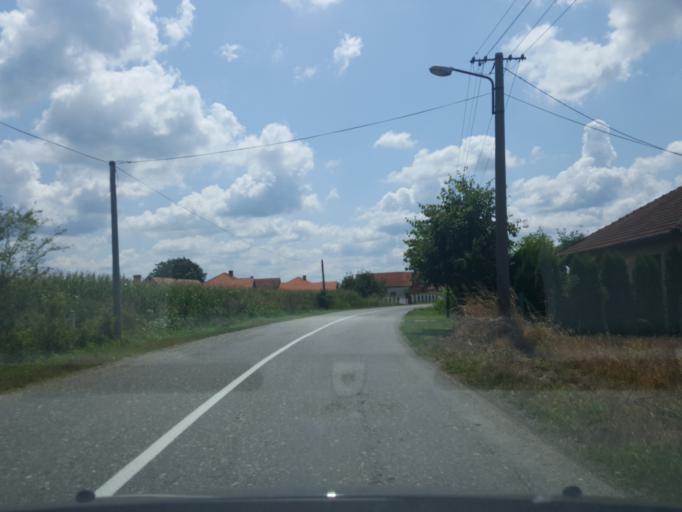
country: RS
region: Central Serbia
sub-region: Macvanski Okrug
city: Bogatic
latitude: 44.8180
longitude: 19.4778
